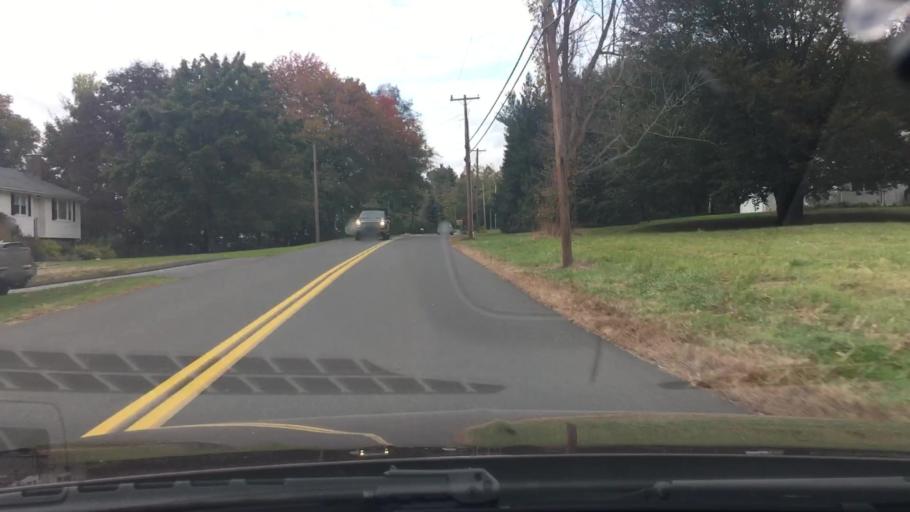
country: US
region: Connecticut
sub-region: Tolland County
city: Ellington
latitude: 41.9264
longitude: -72.4773
